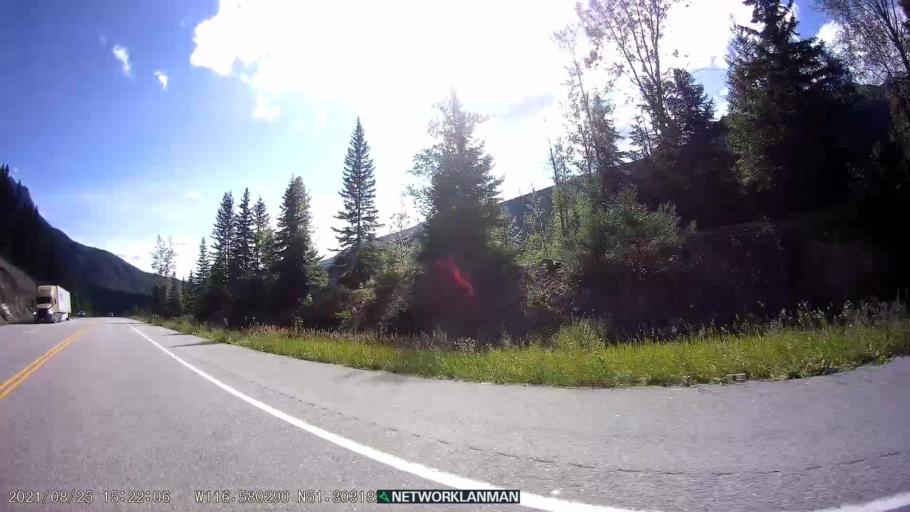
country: CA
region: Alberta
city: Lake Louise
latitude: 51.3027
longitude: -116.5803
